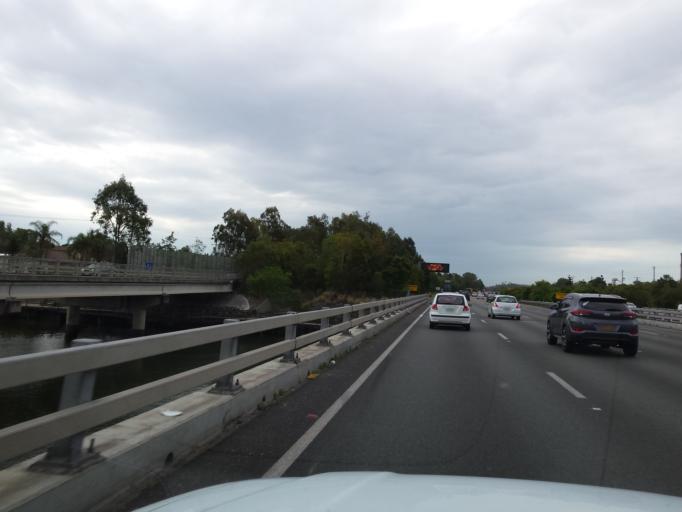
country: AU
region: Queensland
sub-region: Gold Coast
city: Oxenford
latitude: -27.8771
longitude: 153.3143
